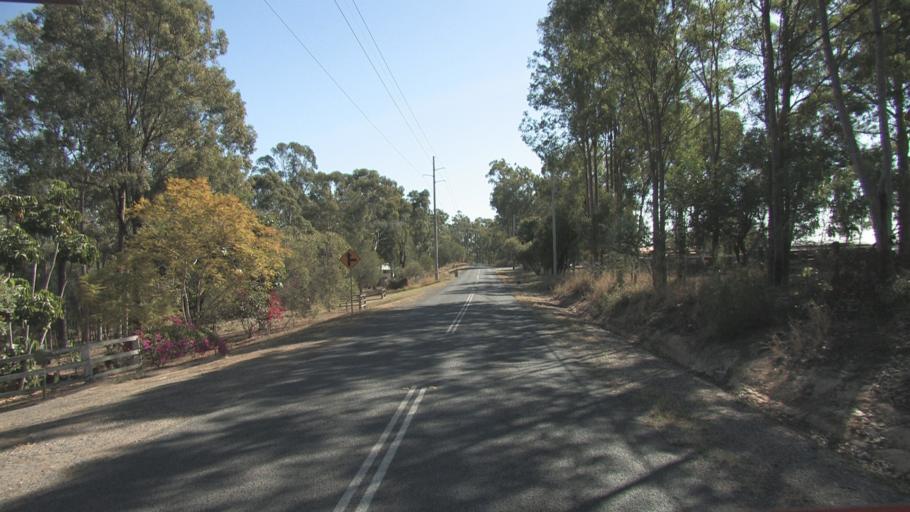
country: AU
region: Queensland
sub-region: Logan
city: Cedar Vale
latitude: -27.8835
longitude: 153.0167
